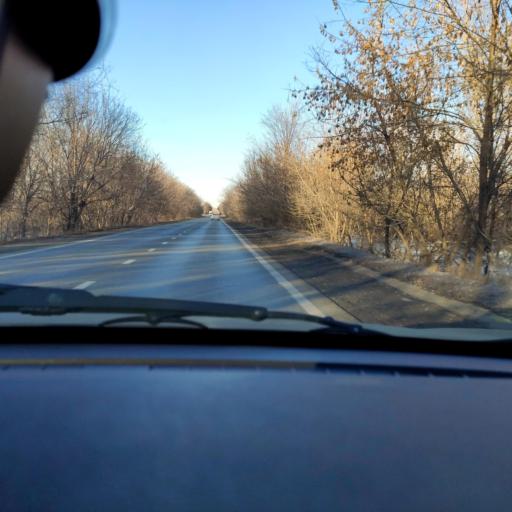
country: RU
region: Samara
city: Tol'yatti
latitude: 53.5473
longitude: 49.3936
